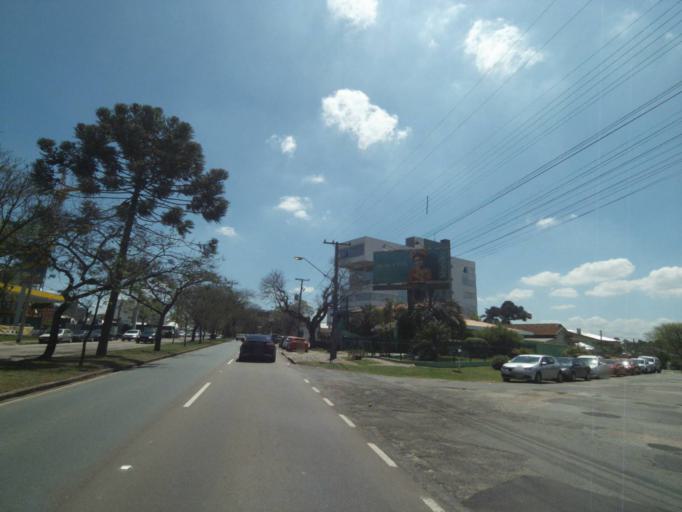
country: BR
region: Parana
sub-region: Curitiba
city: Curitiba
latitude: -25.4106
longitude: -49.2410
